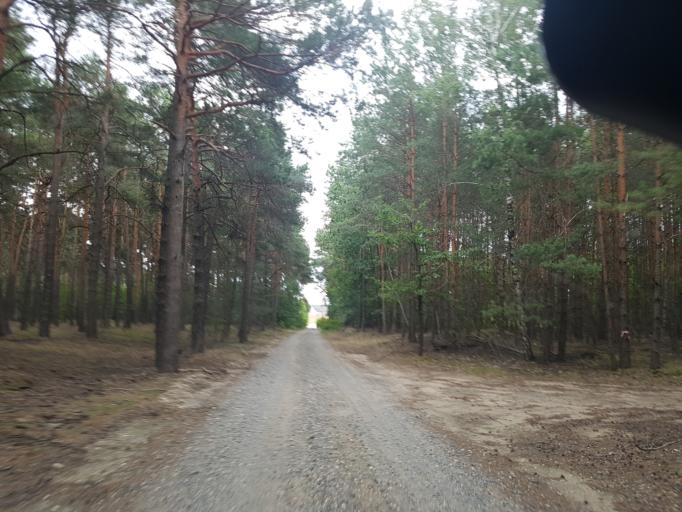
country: DE
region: Brandenburg
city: Sallgast
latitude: 51.6228
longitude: 13.8069
